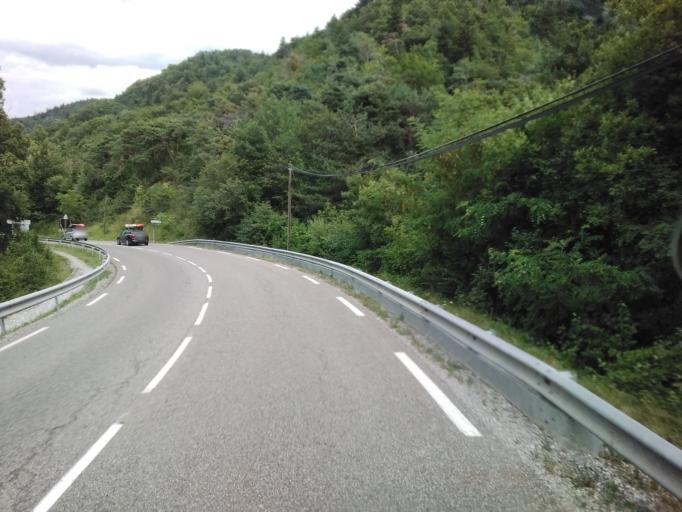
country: FR
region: Provence-Alpes-Cote d'Azur
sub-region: Departement des Hautes-Alpes
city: Embrun
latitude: 44.5226
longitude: 6.3969
